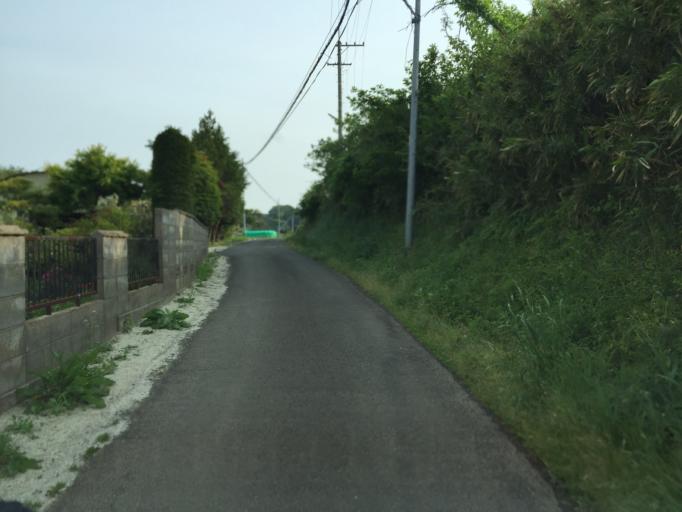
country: JP
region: Fukushima
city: Fukushima-shi
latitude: 37.7175
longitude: 140.4294
